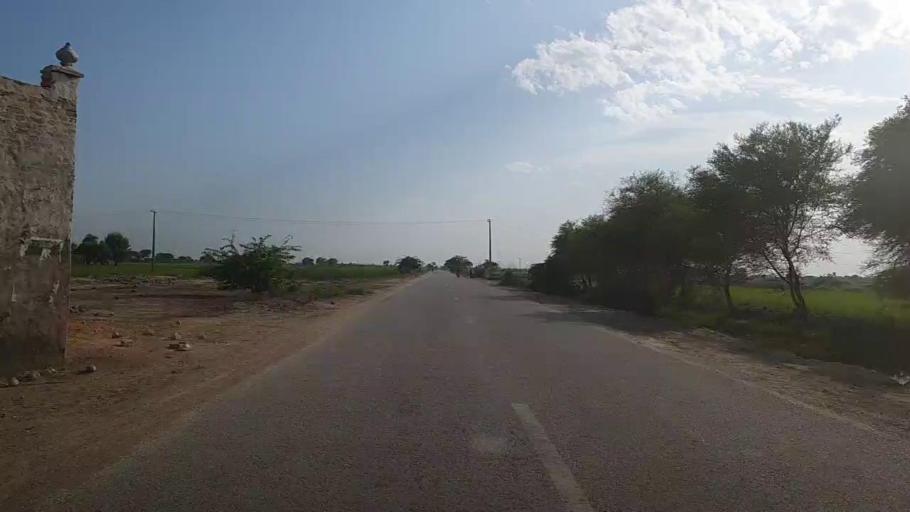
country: PK
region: Sindh
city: Thul
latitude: 28.2097
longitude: 68.7487
